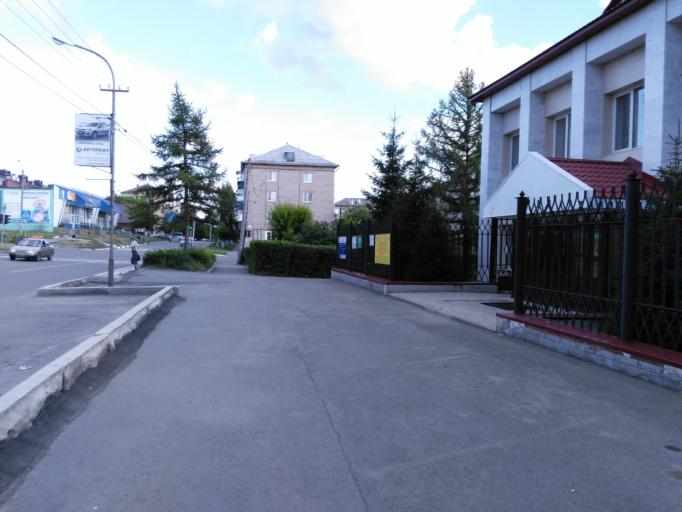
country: RU
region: Bashkortostan
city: Uchaly
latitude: 54.3177
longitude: 59.3834
